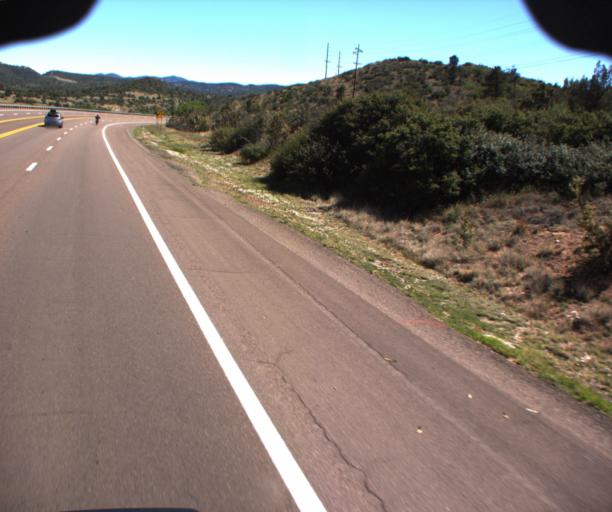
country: US
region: Arizona
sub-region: Yavapai County
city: Prescott
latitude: 34.5884
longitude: -112.4245
